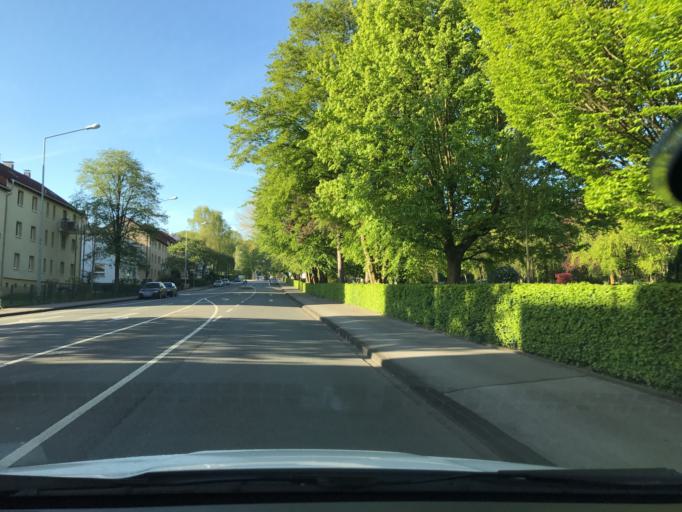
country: DE
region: North Rhine-Westphalia
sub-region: Regierungsbezirk Arnsberg
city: Schwelm
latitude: 51.2826
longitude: 7.2781
